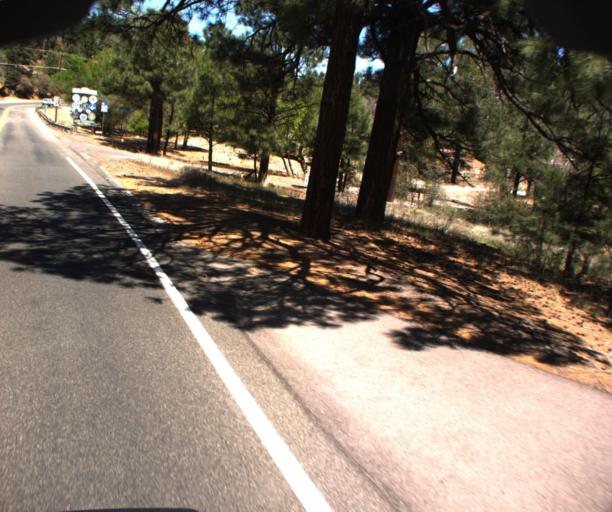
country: US
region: Arizona
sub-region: Yavapai County
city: Prescott
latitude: 34.5127
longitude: -112.4772
